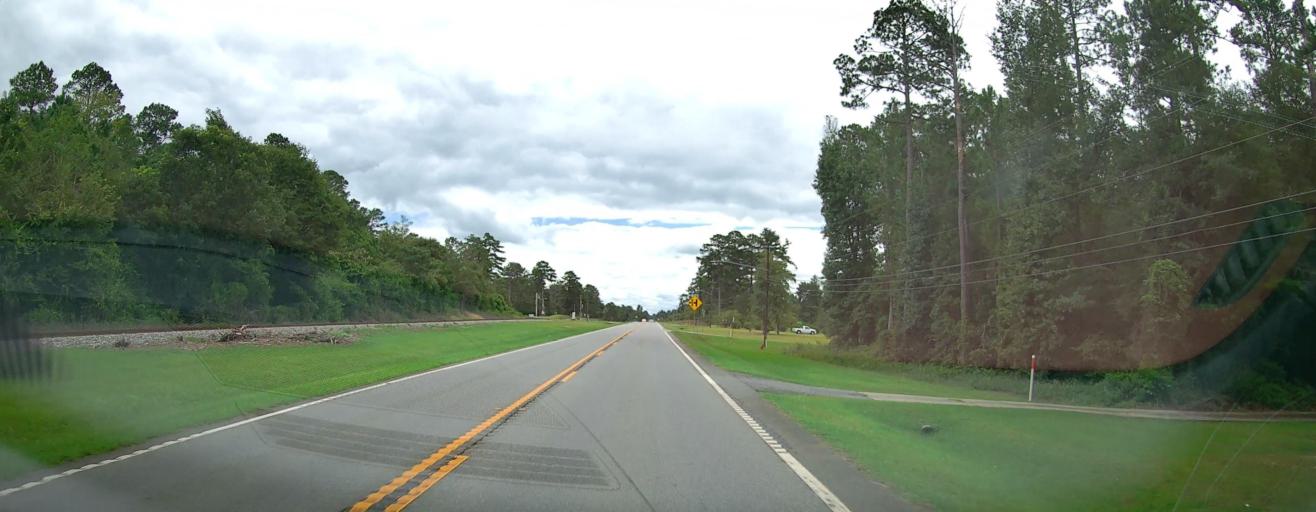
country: US
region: Georgia
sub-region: Twiggs County
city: Jeffersonville
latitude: 32.6811
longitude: -83.3384
